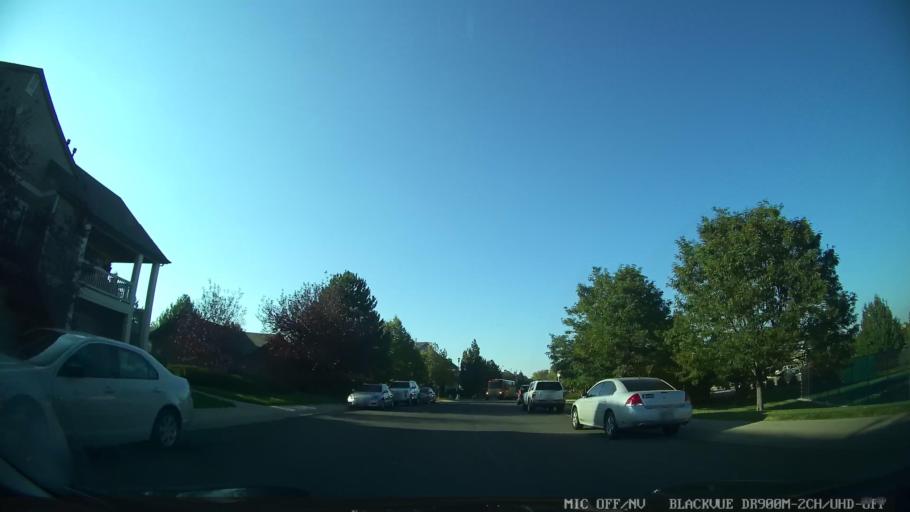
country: US
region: Colorado
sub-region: Larimer County
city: Fort Collins
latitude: 40.5134
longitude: -105.0403
